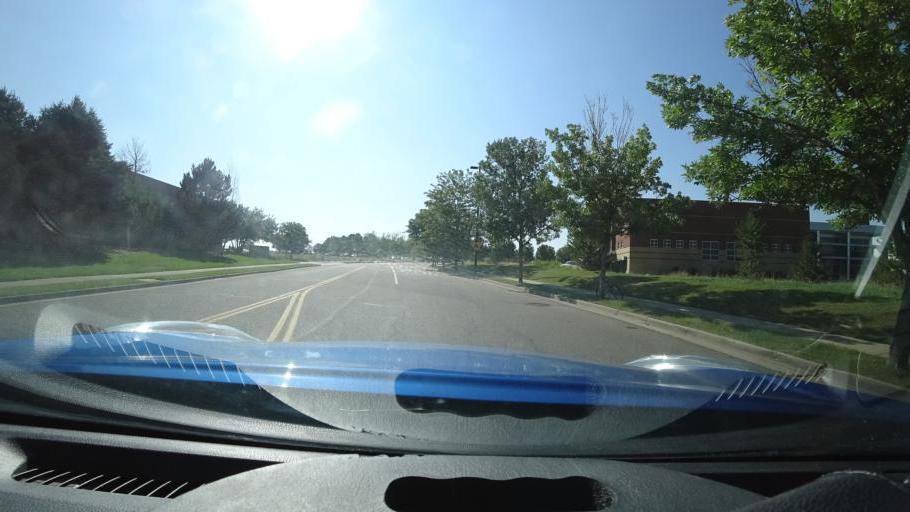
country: US
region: Colorado
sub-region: Adams County
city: Aurora
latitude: 39.7211
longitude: -104.8052
